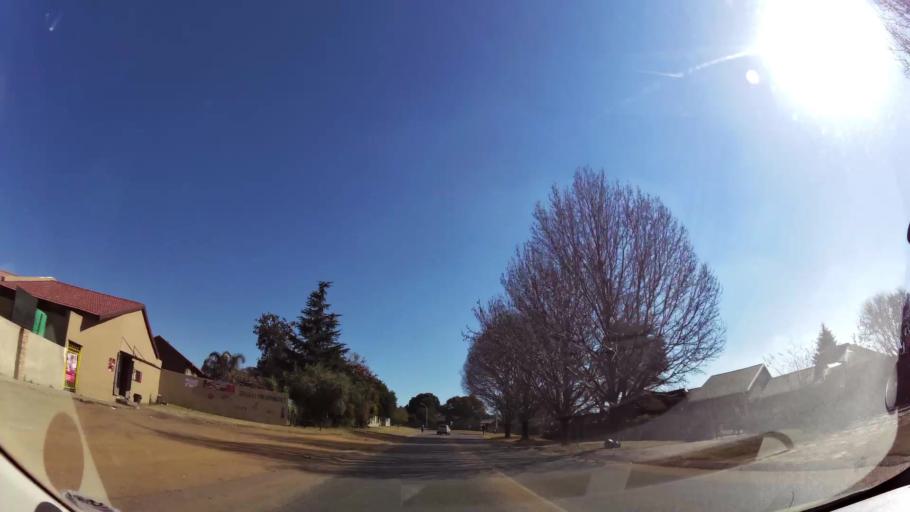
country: ZA
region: Mpumalanga
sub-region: Nkangala District Municipality
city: Witbank
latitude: -25.8337
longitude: 29.2437
